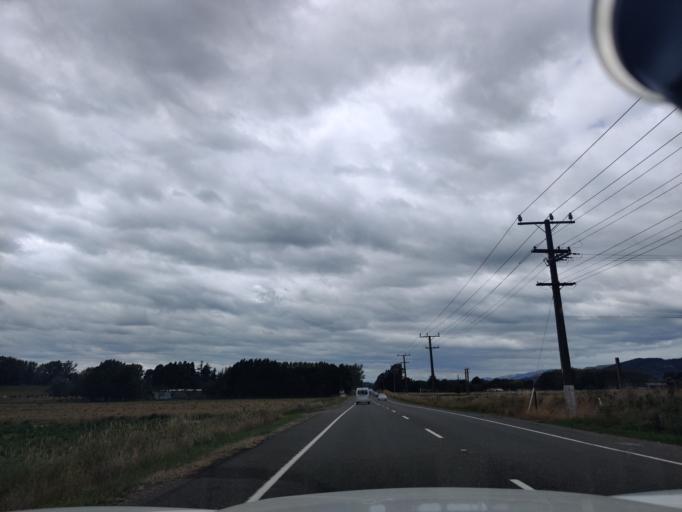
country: NZ
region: Manawatu-Wanganui
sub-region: Horowhenua District
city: Levin
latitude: -40.6224
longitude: 175.3147
